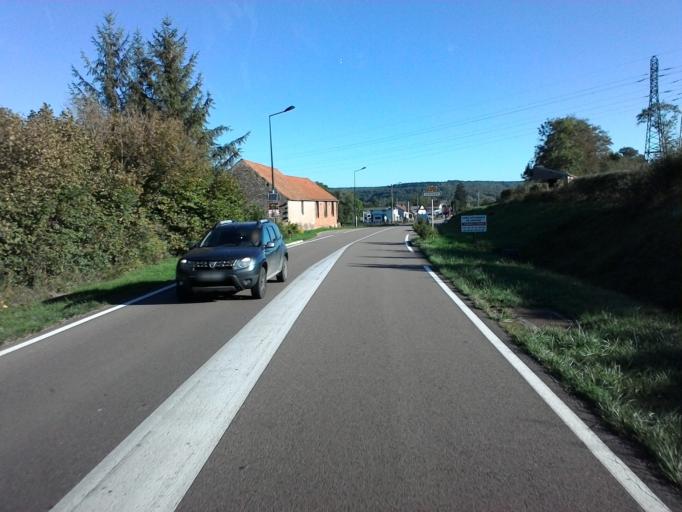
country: FR
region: Bourgogne
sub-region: Departement de la Cote-d'Or
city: Montbard
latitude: 47.6137
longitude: 4.3164
